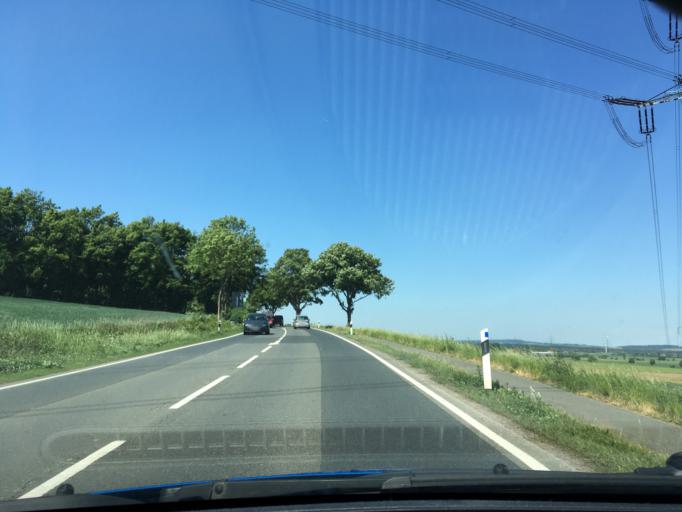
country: DE
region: Lower Saxony
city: Beckedorf
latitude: 52.3355
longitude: 9.3306
